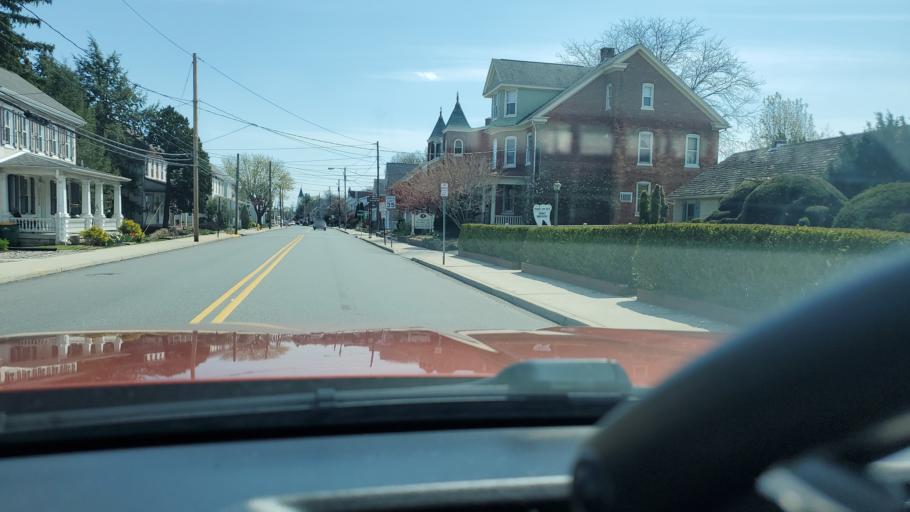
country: US
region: Pennsylvania
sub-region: Montgomery County
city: Pennsburg
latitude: 40.3953
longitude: -75.4955
